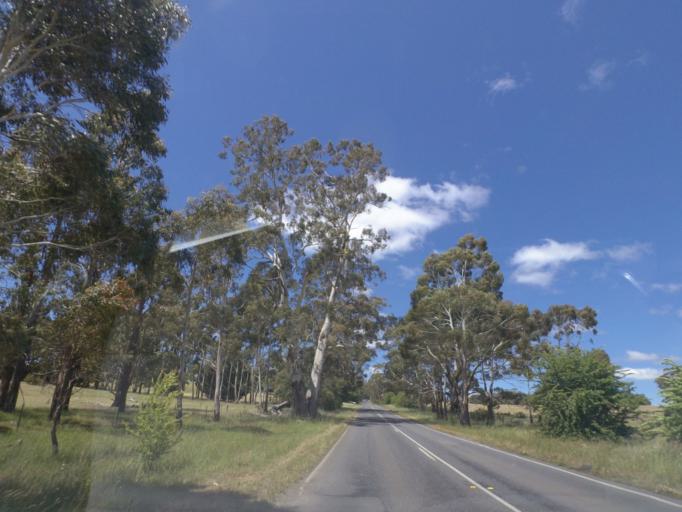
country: AU
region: Victoria
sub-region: Mount Alexander
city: Castlemaine
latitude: -37.2915
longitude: 144.2565
